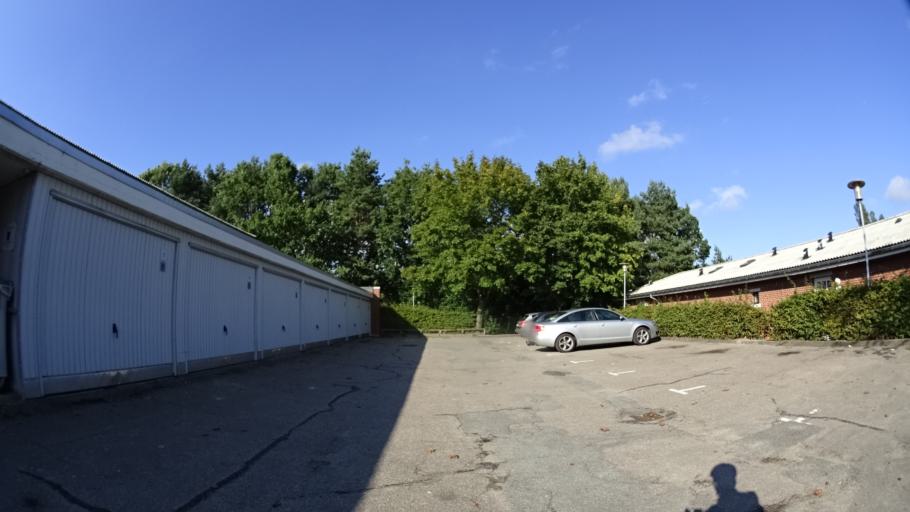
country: DK
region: Central Jutland
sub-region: Arhus Kommune
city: Marslet
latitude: 56.1108
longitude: 10.1693
